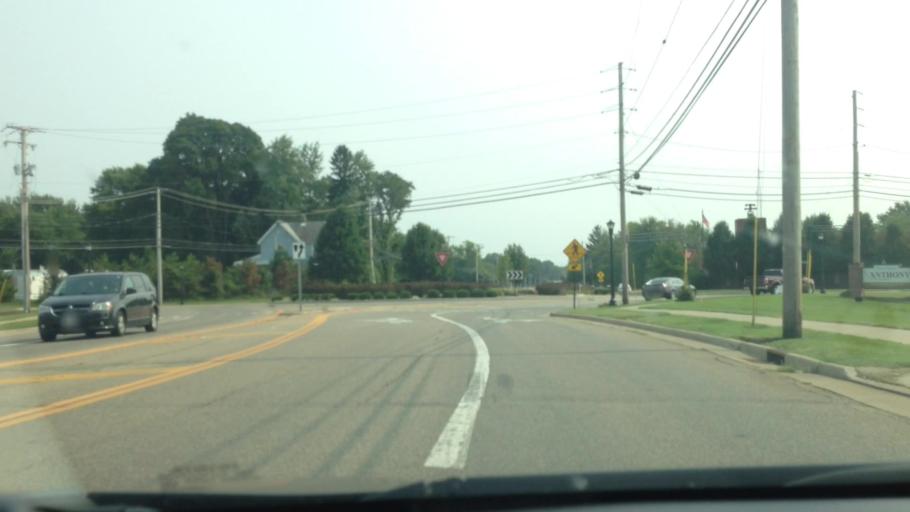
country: US
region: Ohio
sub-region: Summit County
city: Greensburg
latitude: 40.9483
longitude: -81.4655
